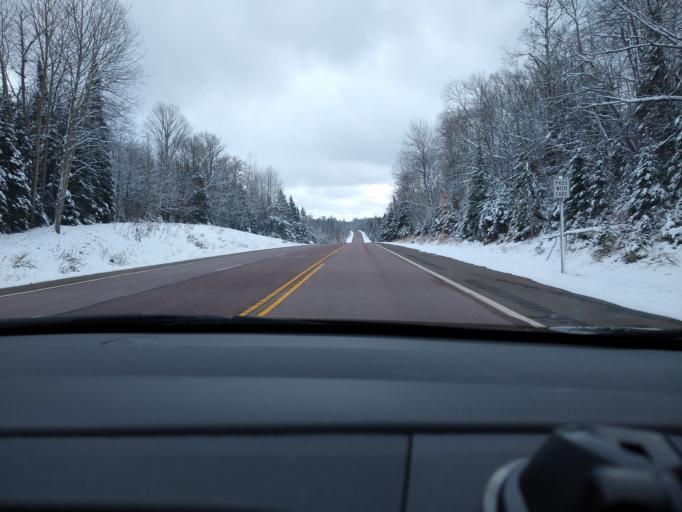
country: US
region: Michigan
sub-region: Iron County
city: Iron River
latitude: 46.1776
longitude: -88.9538
